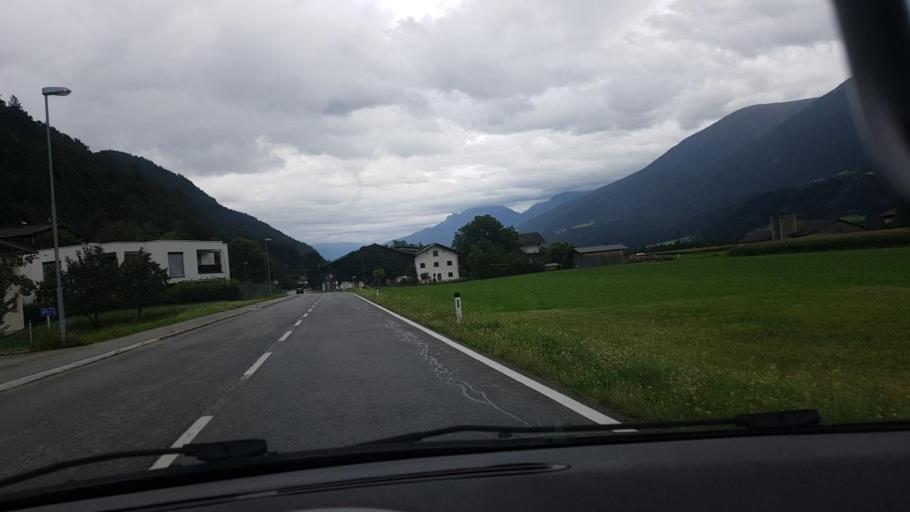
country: AT
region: Tyrol
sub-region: Politischer Bezirk Innsbruck Land
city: Pettnau
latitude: 47.3026
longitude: 11.1318
